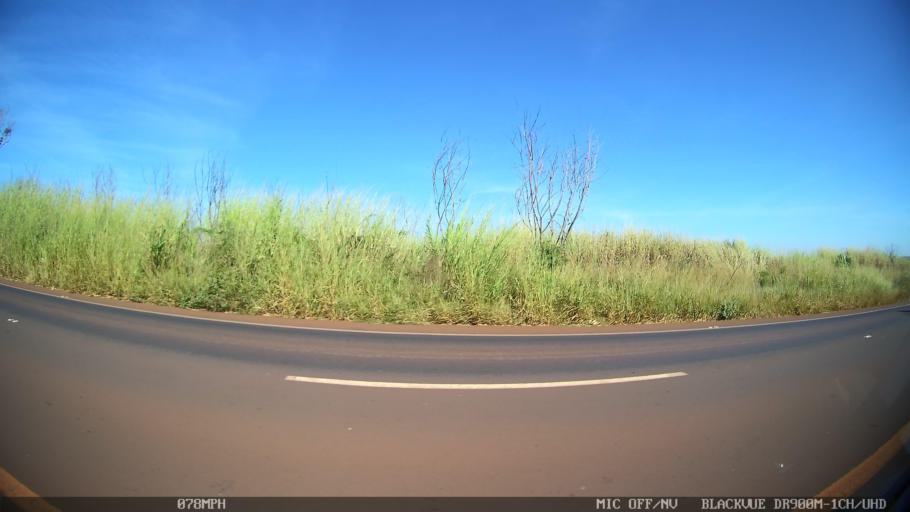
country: BR
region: Sao Paulo
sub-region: Sao Joaquim Da Barra
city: Sao Joaquim da Barra
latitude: -20.5426
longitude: -47.7970
